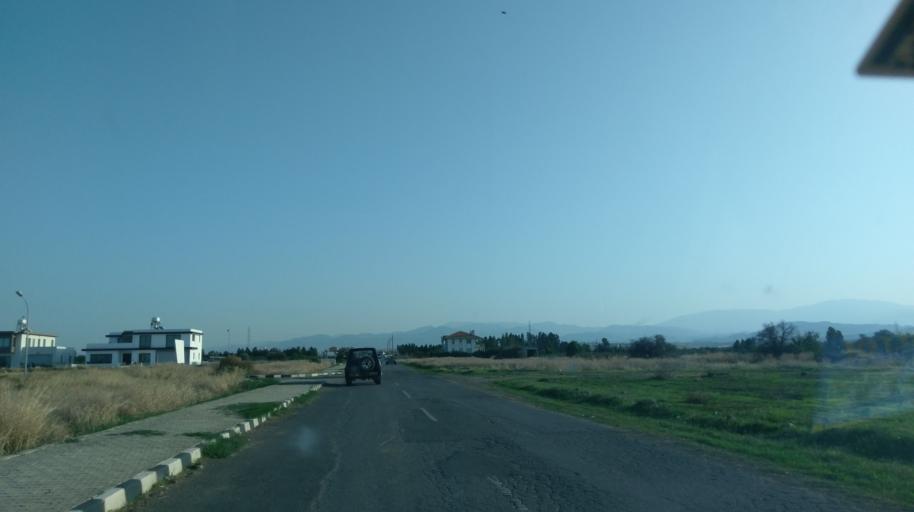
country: CY
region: Lefkosia
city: Lefka
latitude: 35.1575
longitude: 32.9044
